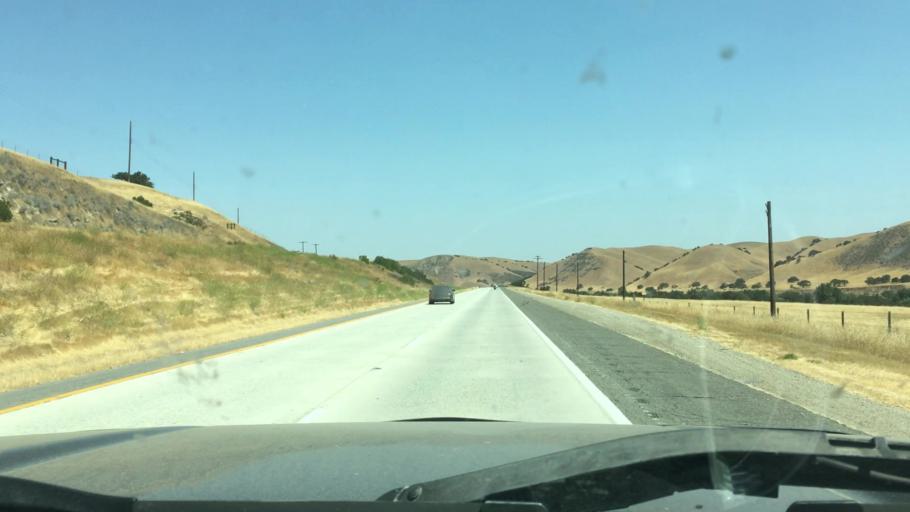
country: US
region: California
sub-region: San Luis Obispo County
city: Lake Nacimiento
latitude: 35.8931
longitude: -120.8415
